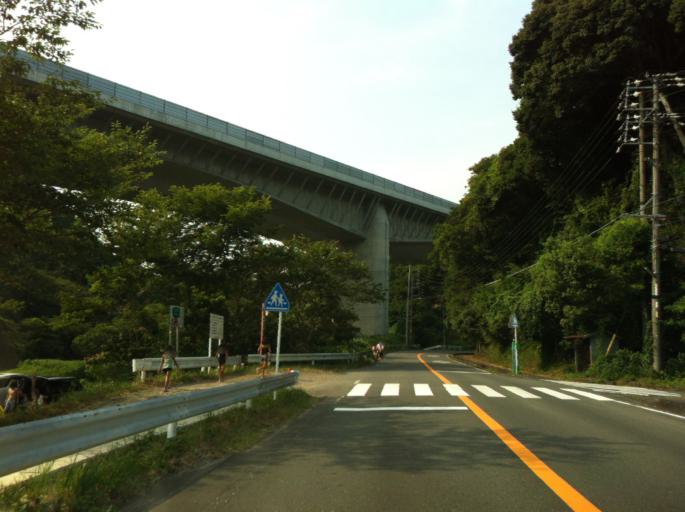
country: JP
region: Shizuoka
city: Fujieda
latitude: 34.9234
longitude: 138.2713
